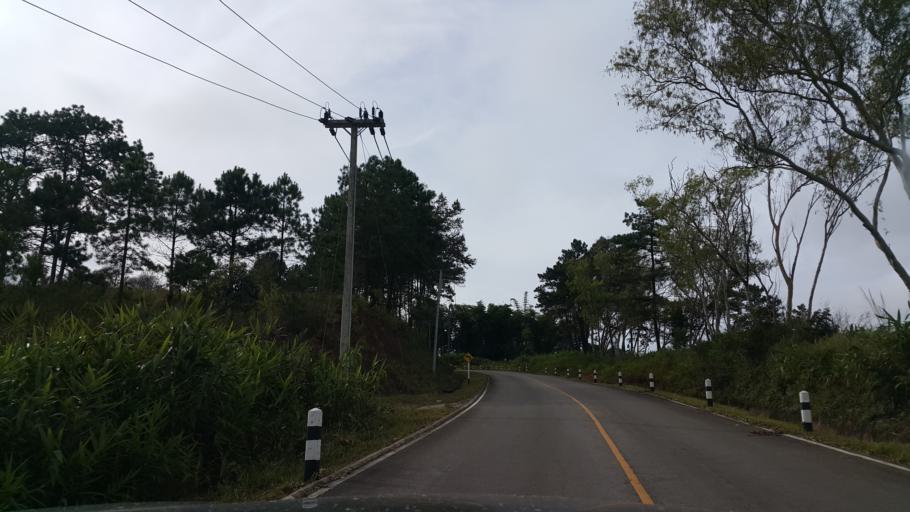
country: TH
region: Chiang Mai
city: Chaem Luang
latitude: 18.9501
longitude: 98.4491
